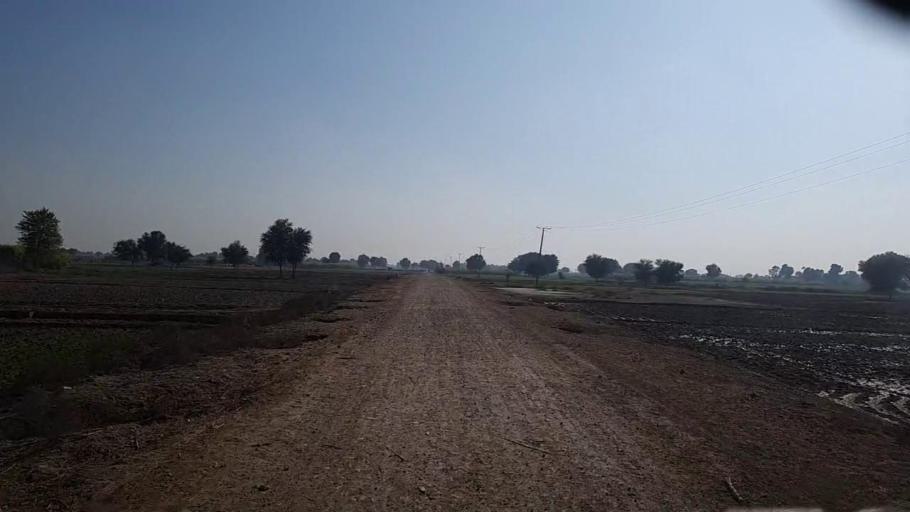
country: PK
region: Sindh
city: Darya Khan Marri
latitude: 26.6626
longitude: 68.3363
